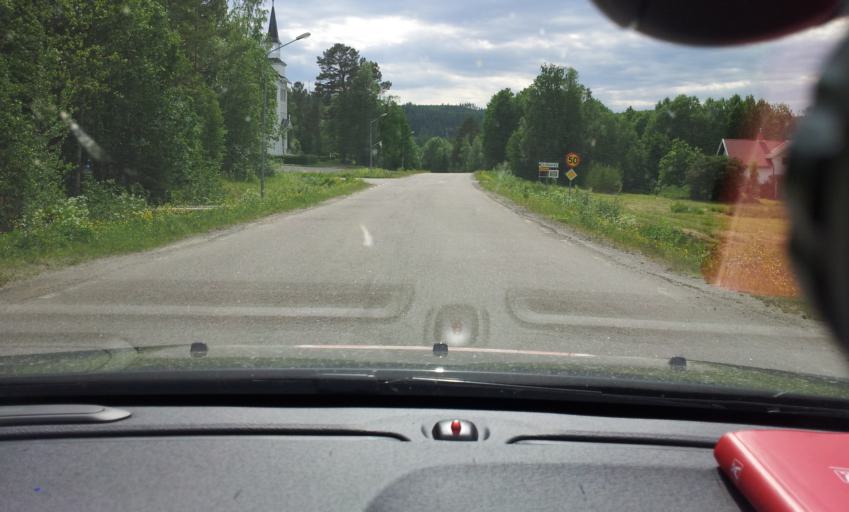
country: SE
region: Jaemtland
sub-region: Bergs Kommun
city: Hoverberg
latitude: 62.6652
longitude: 14.7501
